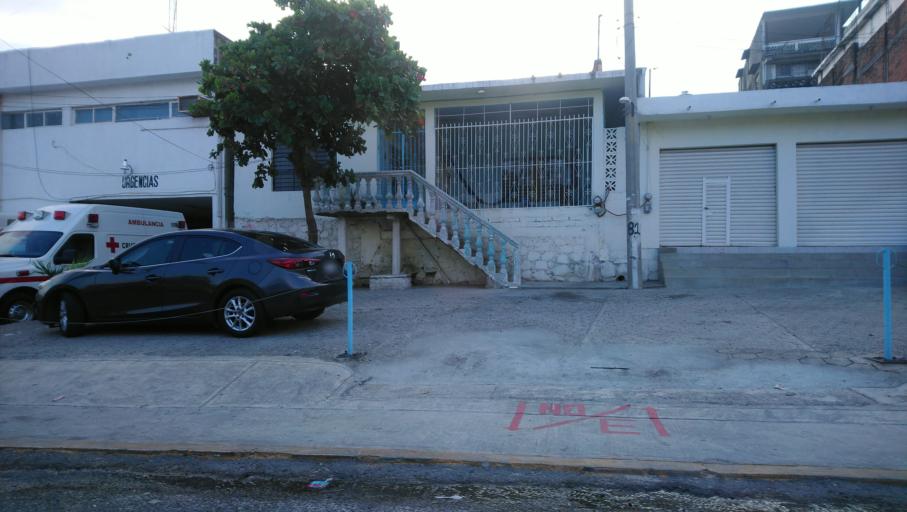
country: MX
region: Oaxaca
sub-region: Salina Cruz
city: Salina Cruz
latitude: 16.1982
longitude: -95.2017
